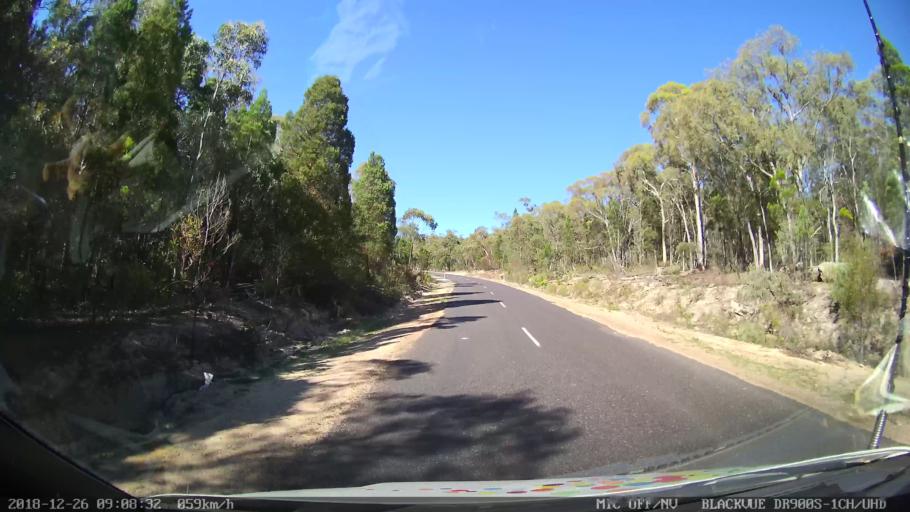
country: AU
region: New South Wales
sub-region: Mid-Western Regional
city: Kandos
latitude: -32.7168
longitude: 150.0014
